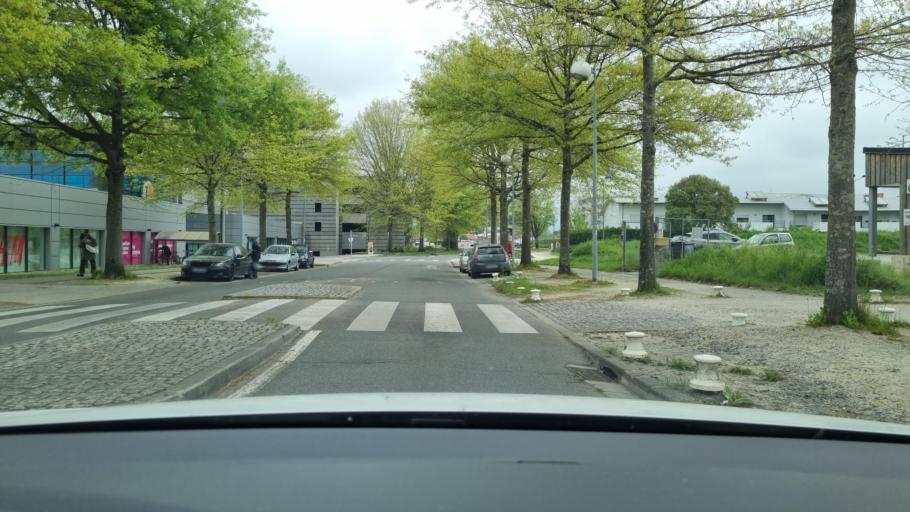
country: FR
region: Aquitaine
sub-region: Departement des Pyrenees-Atlantiques
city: Pau
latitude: 43.3154
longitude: -0.3570
